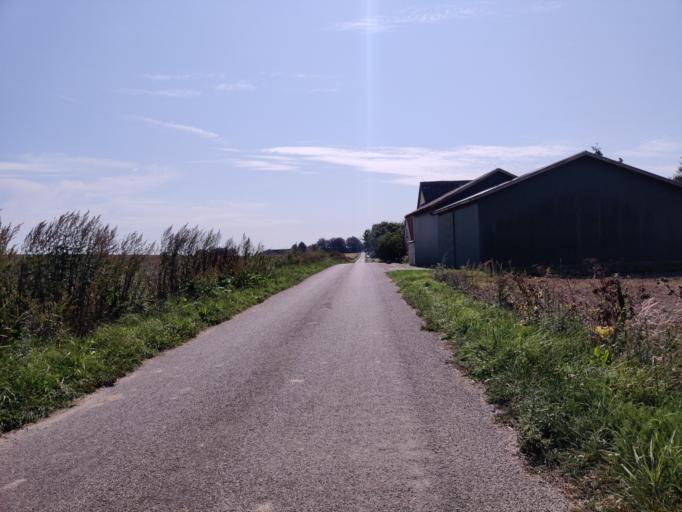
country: DK
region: Zealand
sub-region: Guldborgsund Kommune
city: Nykobing Falster
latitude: 54.6823
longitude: 11.8917
